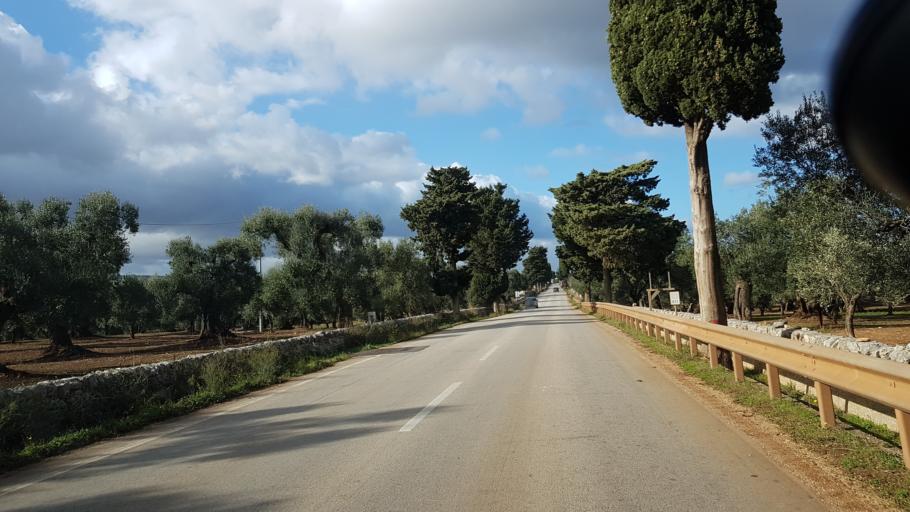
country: IT
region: Apulia
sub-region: Provincia di Brindisi
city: Montalbano
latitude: 40.7764
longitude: 17.4937
